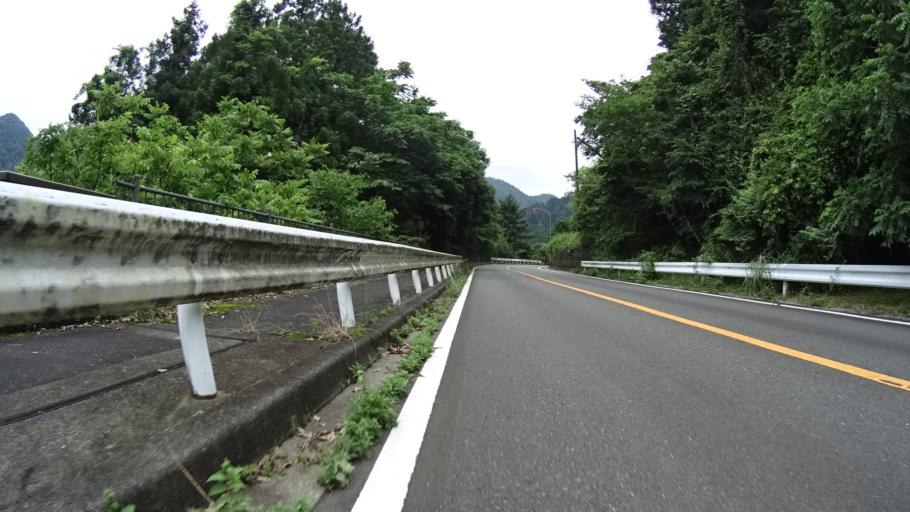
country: JP
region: Kanagawa
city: Hadano
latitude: 35.5073
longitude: 139.2309
